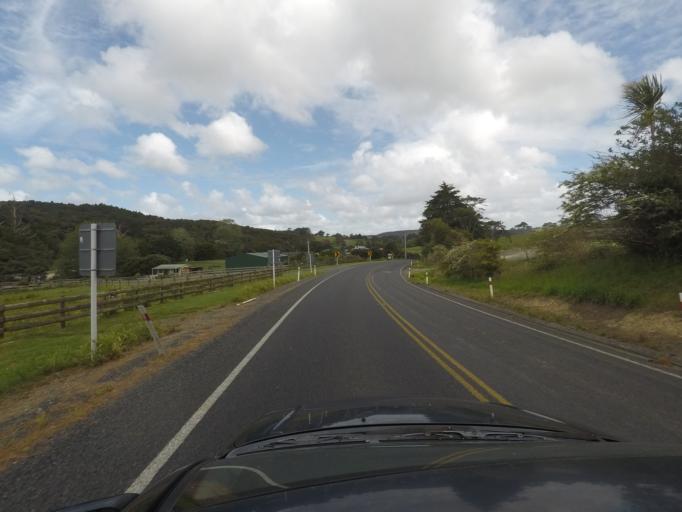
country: NZ
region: Auckland
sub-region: Auckland
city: Parakai
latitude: -36.6483
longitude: 174.5194
